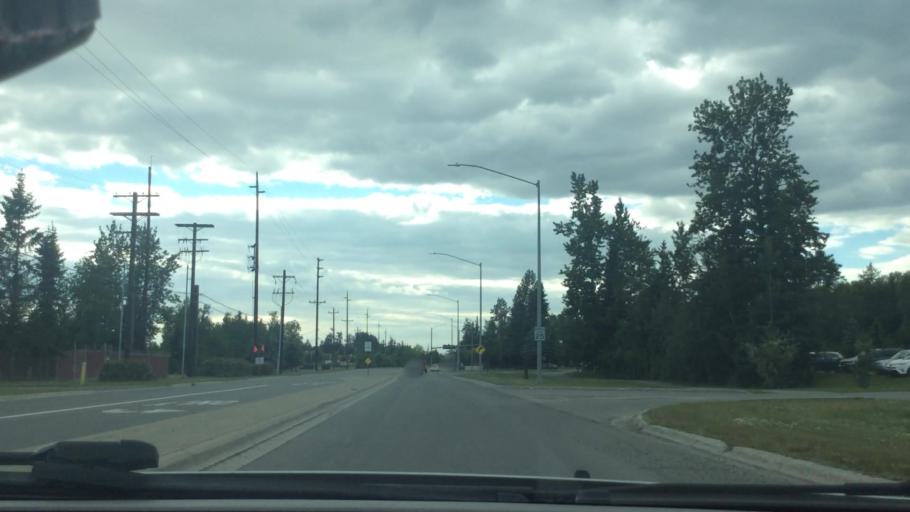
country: US
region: Alaska
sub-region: Anchorage Municipality
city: Elmendorf Air Force Base
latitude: 61.2315
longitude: -149.7625
